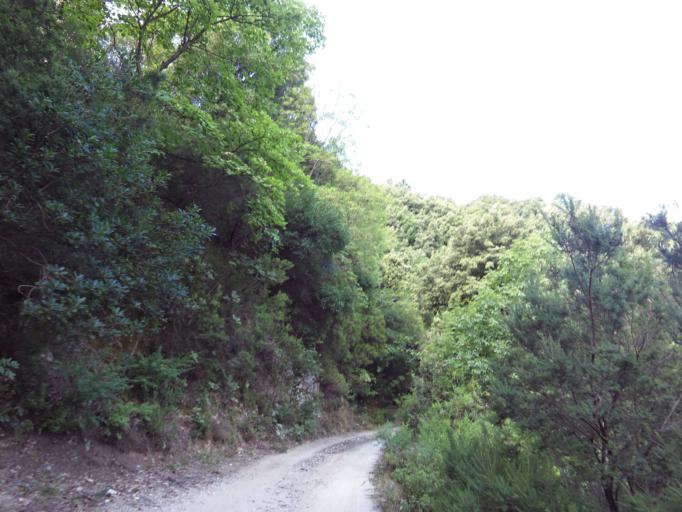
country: IT
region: Calabria
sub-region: Provincia di Reggio Calabria
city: Bivongi
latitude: 38.4953
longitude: 16.4036
